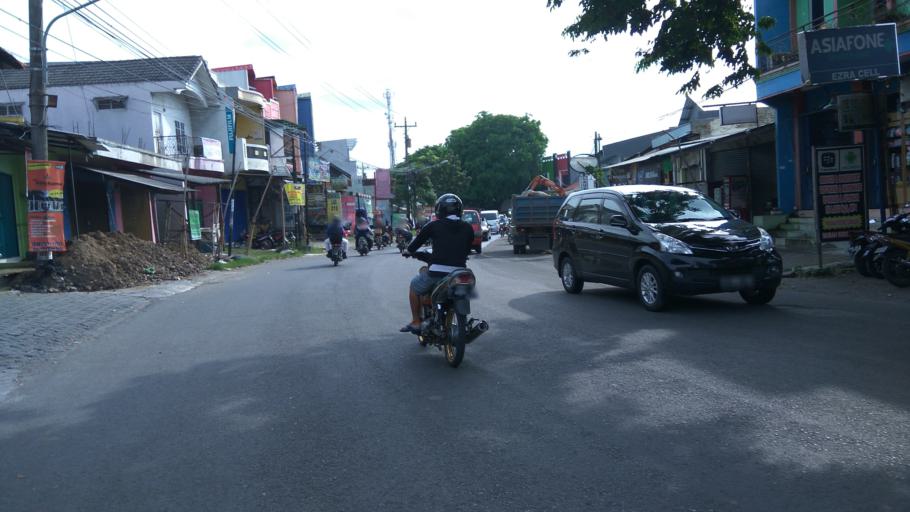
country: ID
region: Central Java
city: Mranggen
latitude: -7.0210
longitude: 110.4702
